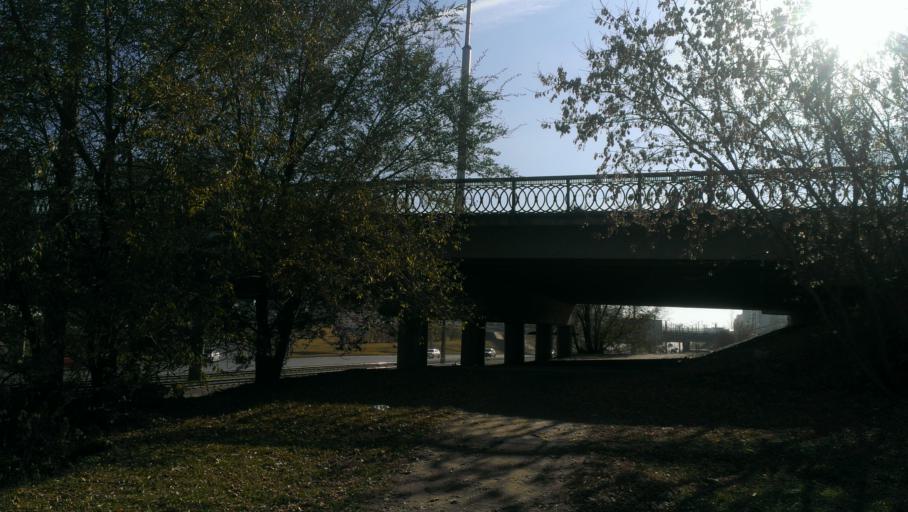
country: RU
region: Altai Krai
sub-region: Gorod Barnaulskiy
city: Barnaul
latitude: 53.3430
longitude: 83.6951
